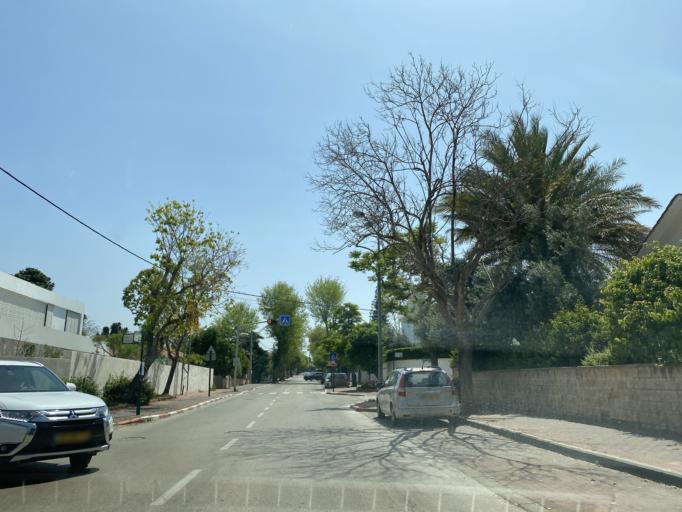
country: IL
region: Central District
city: Ra'anana
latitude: 32.1869
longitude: 34.8732
